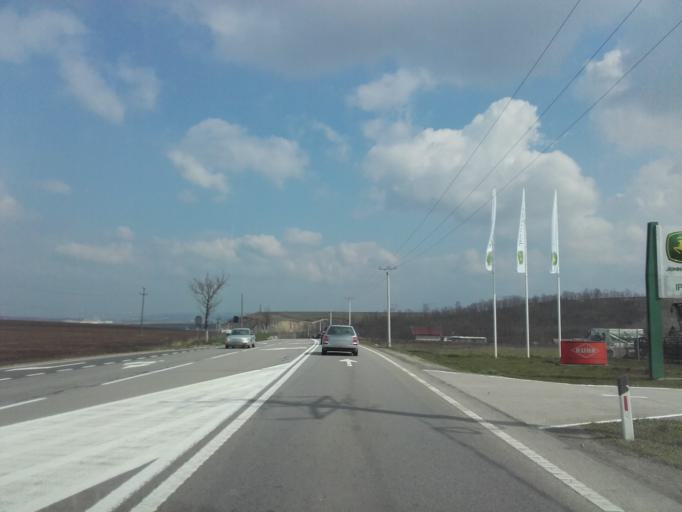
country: RO
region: Mures
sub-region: Comuna Sanpaul
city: Valea Izvoarelor
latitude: 46.4516
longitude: 24.3690
